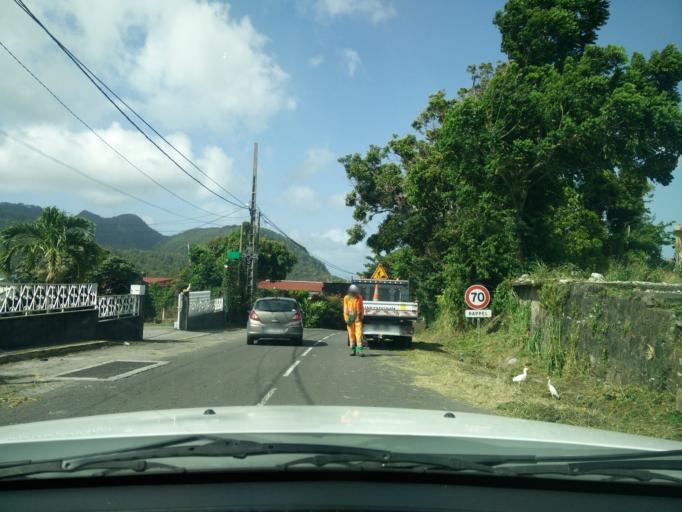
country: GP
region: Guadeloupe
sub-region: Guadeloupe
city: Gourbeyre
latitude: 15.9984
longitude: -61.7008
